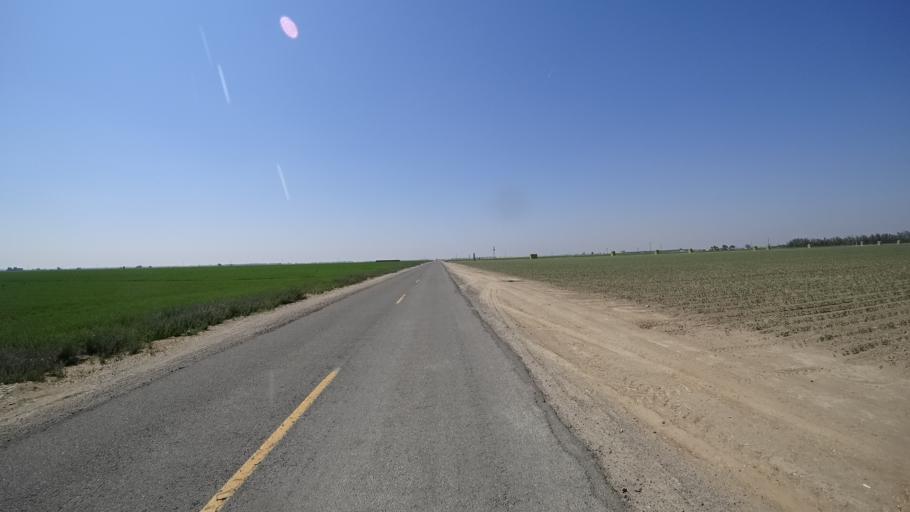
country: US
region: California
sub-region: Tulare County
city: Goshen
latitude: 36.3786
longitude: -119.5290
